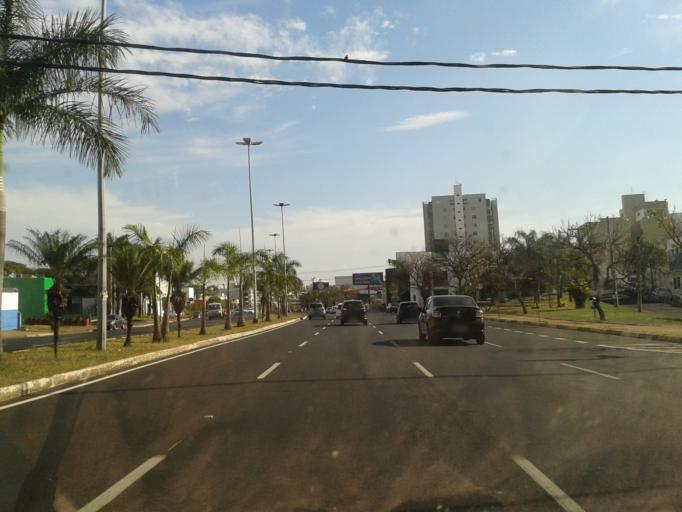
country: BR
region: Minas Gerais
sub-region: Uberlandia
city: Uberlandia
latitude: -18.9258
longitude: -48.2731
